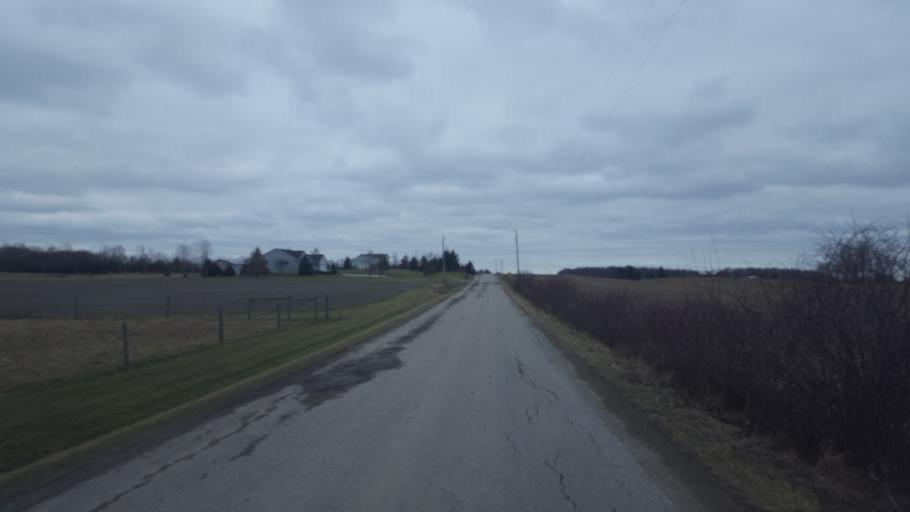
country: US
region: Ohio
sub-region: Morrow County
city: Mount Gilead
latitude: 40.5939
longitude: -82.7478
